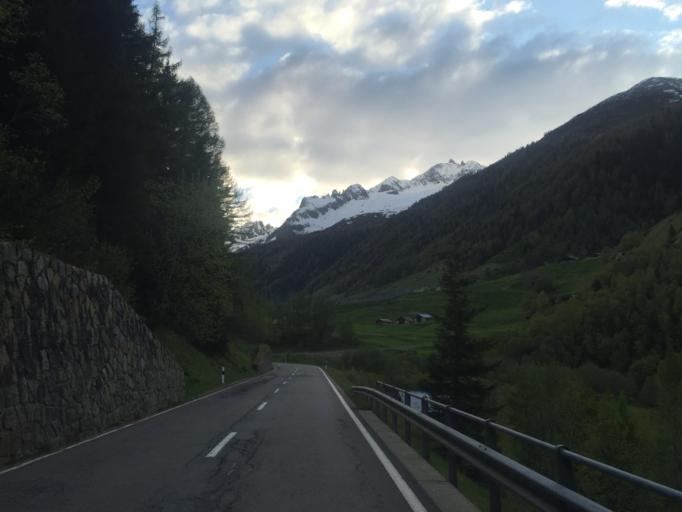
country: CH
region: Ticino
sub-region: Leventina District
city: Airolo
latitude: 46.5111
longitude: 8.5326
